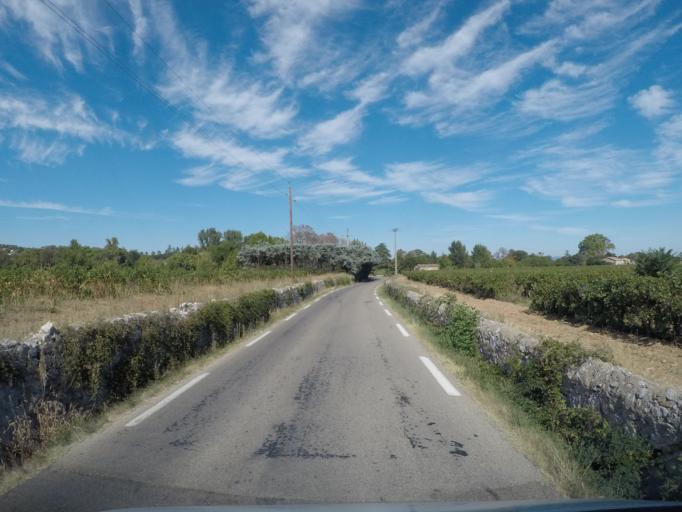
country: FR
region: Languedoc-Roussillon
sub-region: Departement du Gard
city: Boisset-et-Gaujac
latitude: 44.0169
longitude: 3.9927
